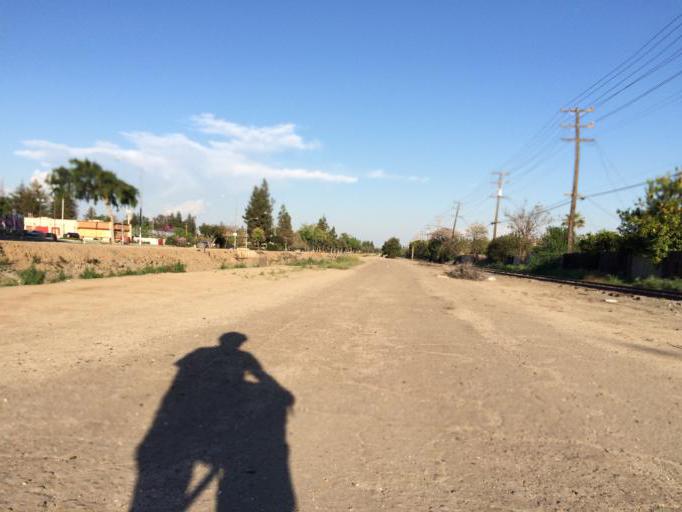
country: US
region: California
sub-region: Fresno County
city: Sunnyside
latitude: 36.7648
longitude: -119.7329
